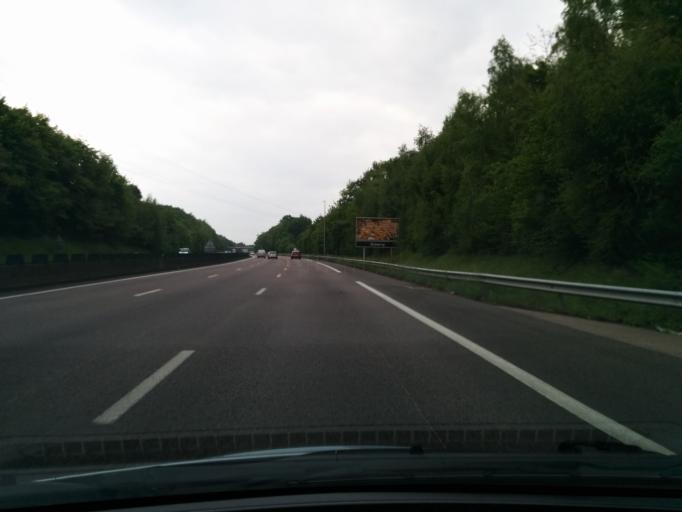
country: FR
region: Ile-de-France
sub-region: Departement des Yvelines
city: Rosny-sur-Seine
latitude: 48.9989
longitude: 1.6134
